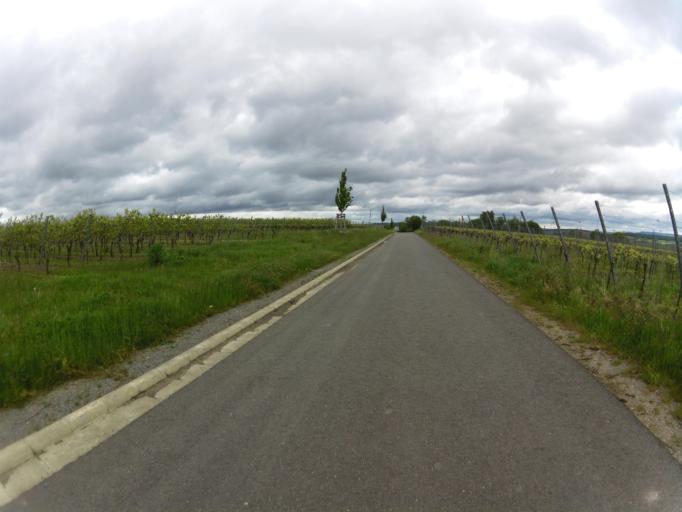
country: DE
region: Bavaria
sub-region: Regierungsbezirk Unterfranken
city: Sommerach
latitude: 49.8424
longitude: 10.2054
